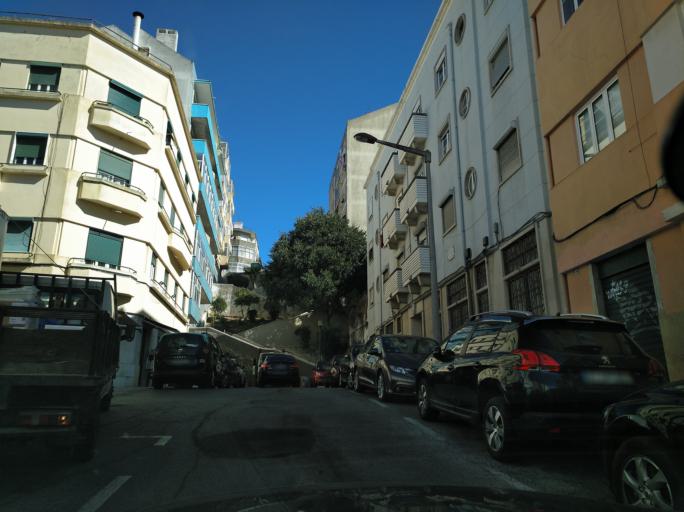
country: PT
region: Lisbon
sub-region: Lisbon
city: Lisbon
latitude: 38.7385
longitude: -9.1301
